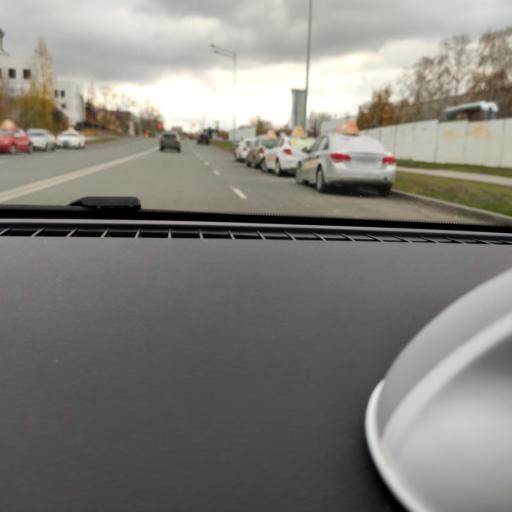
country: RU
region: Samara
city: Samara
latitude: 53.2111
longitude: 50.1499
